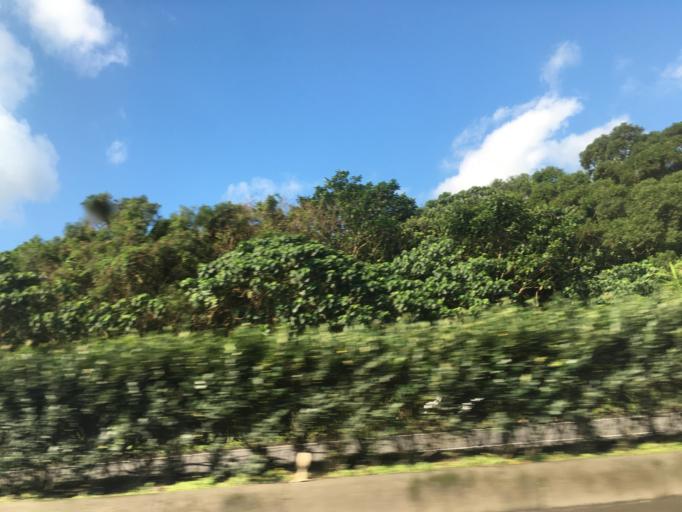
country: TW
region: Taiwan
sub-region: Yilan
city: Yilan
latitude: 24.9315
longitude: 121.8846
